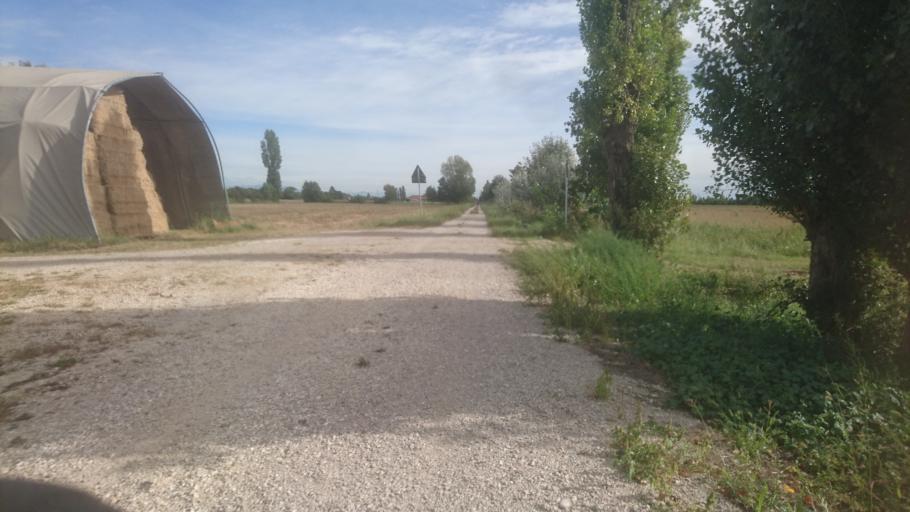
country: IT
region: Veneto
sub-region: Provincia di Vicenza
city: Montegalda
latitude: 45.4689
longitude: 11.6585
